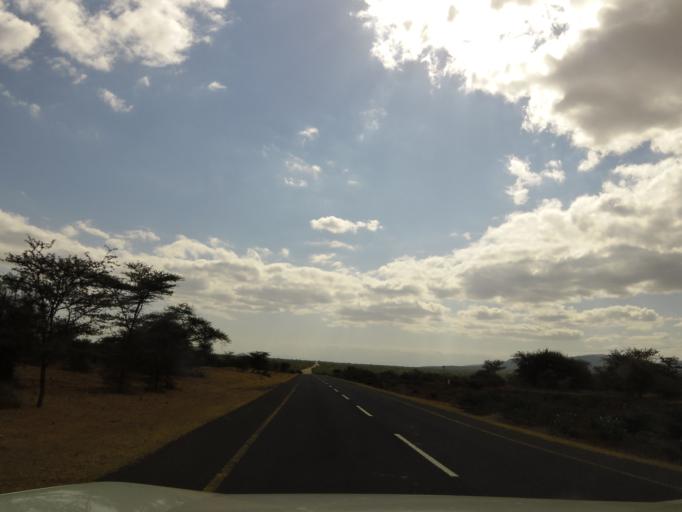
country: TZ
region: Arusha
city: Mto wa Mbu
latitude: -3.5290
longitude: 36.0670
